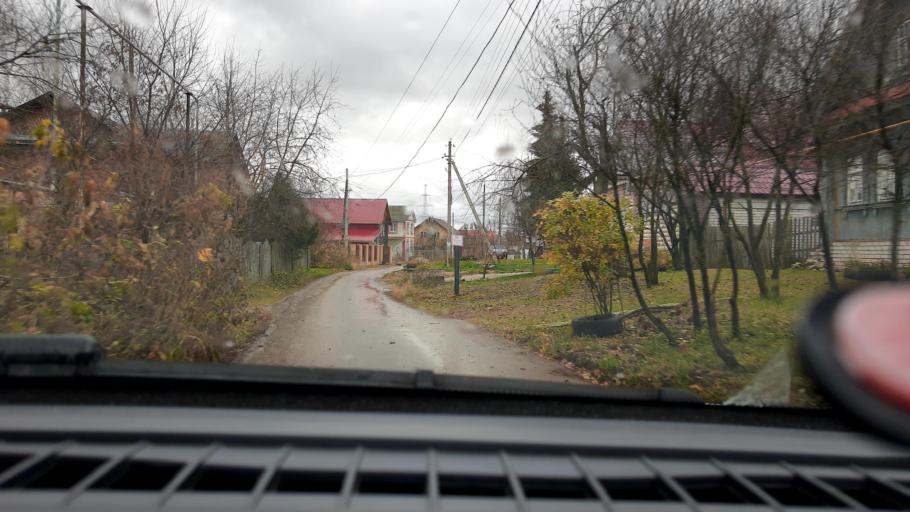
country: RU
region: Nizjnij Novgorod
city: Afonino
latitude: 56.2717
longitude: 44.1072
